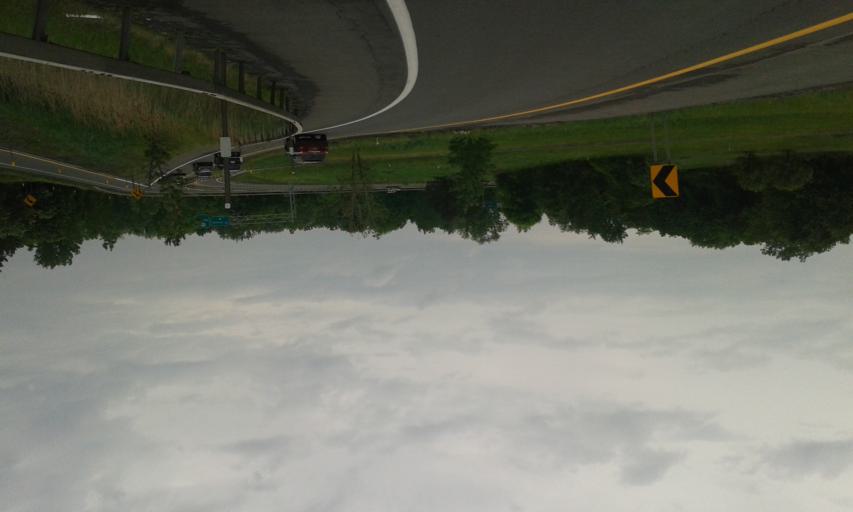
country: US
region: New York
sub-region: Onondaga County
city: Seneca Knolls
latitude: 43.1122
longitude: -76.2872
